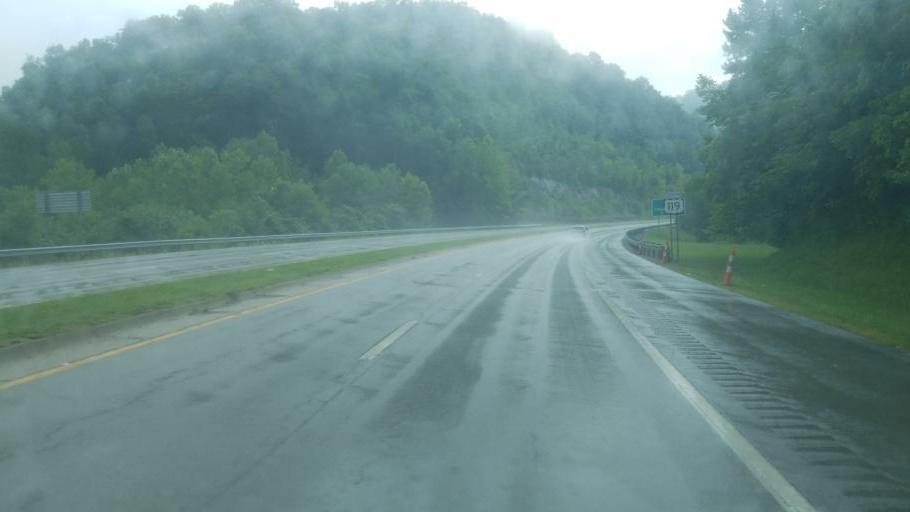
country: US
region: West Virginia
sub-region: Logan County
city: Chapmanville
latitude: 37.9744
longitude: -81.9972
